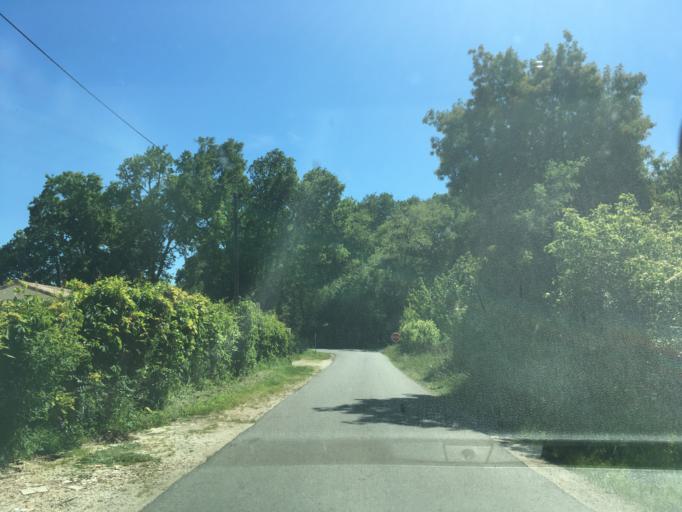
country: FR
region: Aquitaine
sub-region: Departement de la Gironde
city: Lesparre-Medoc
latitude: 45.2963
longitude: -0.8926
